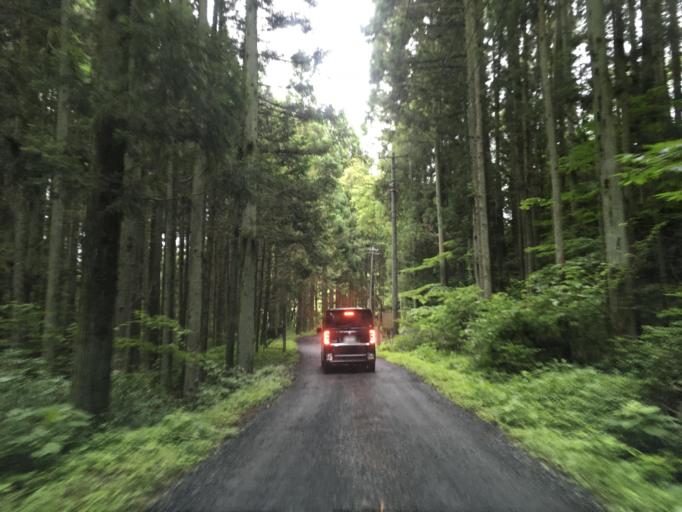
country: JP
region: Iwate
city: Ichinoseki
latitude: 38.7820
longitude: 141.4196
